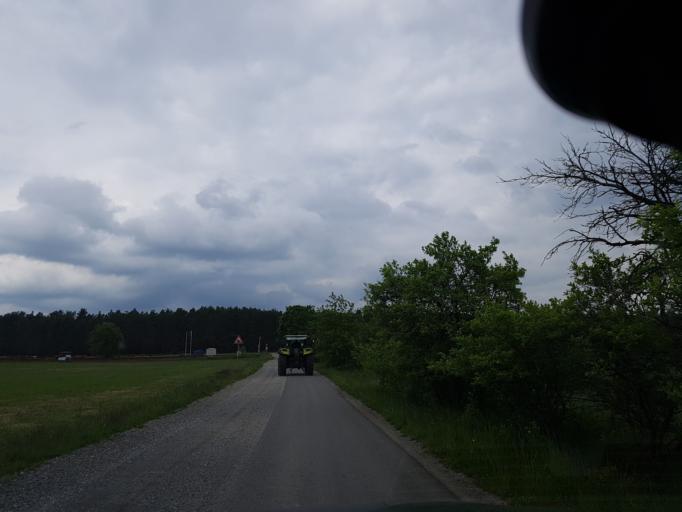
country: DE
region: Brandenburg
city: Crinitz
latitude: 51.6614
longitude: 13.7854
